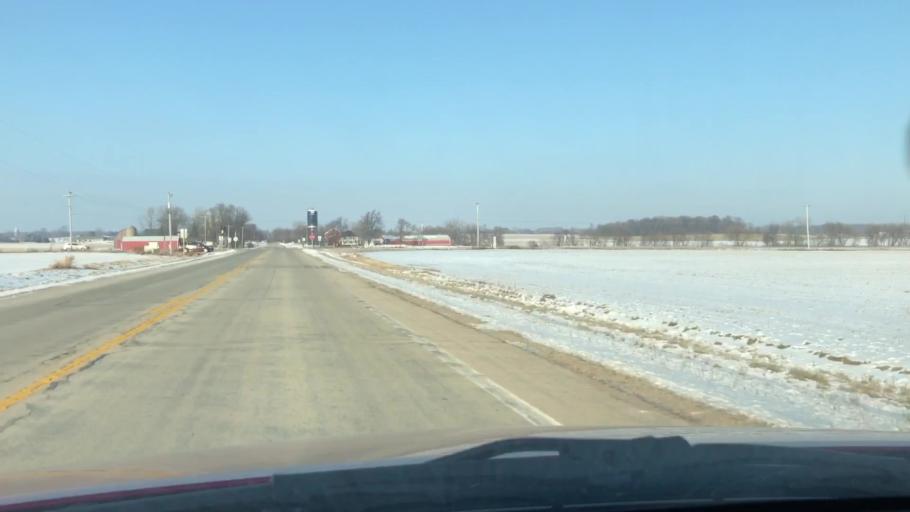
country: US
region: Wisconsin
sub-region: Outagamie County
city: Kimberly
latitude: 44.3853
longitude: -88.3747
